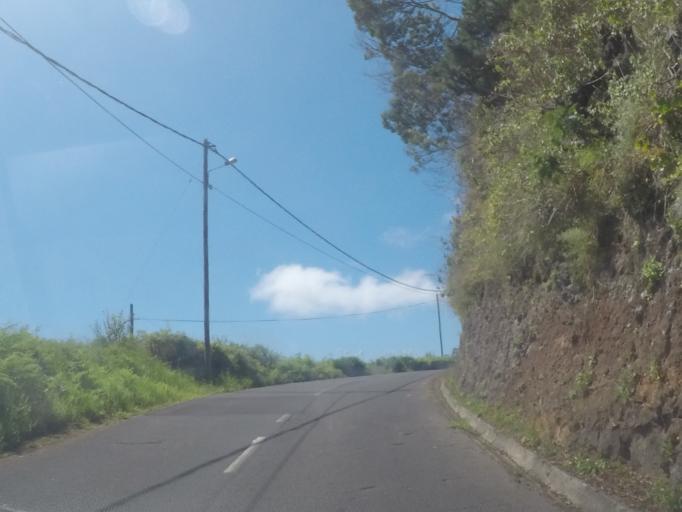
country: PT
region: Madeira
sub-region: Camara de Lobos
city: Curral das Freiras
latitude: 32.6914
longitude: -16.9707
